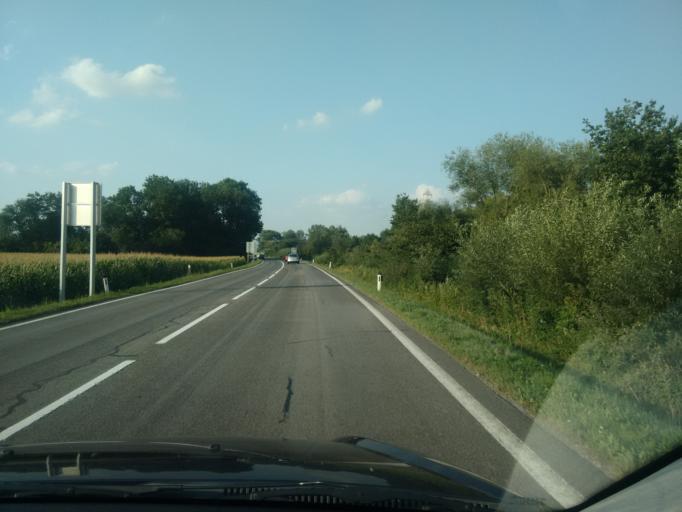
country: AT
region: Upper Austria
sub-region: Politischer Bezirk Linz-Land
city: Asten
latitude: 48.2109
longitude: 14.4016
